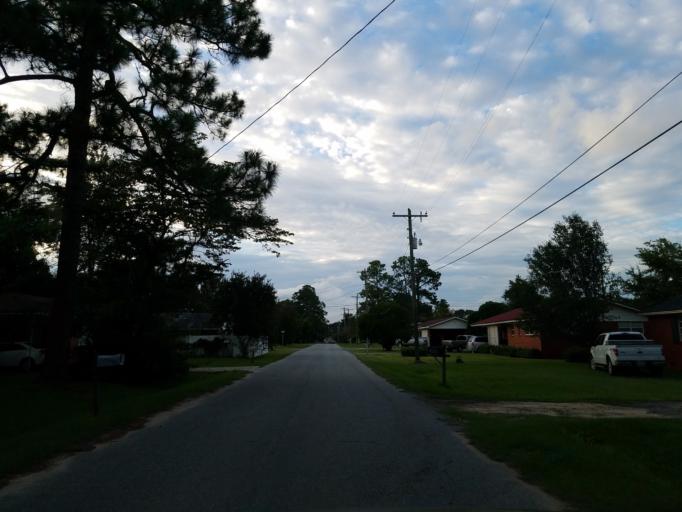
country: US
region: Georgia
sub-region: Cook County
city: Adel
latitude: 31.1445
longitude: -83.4223
